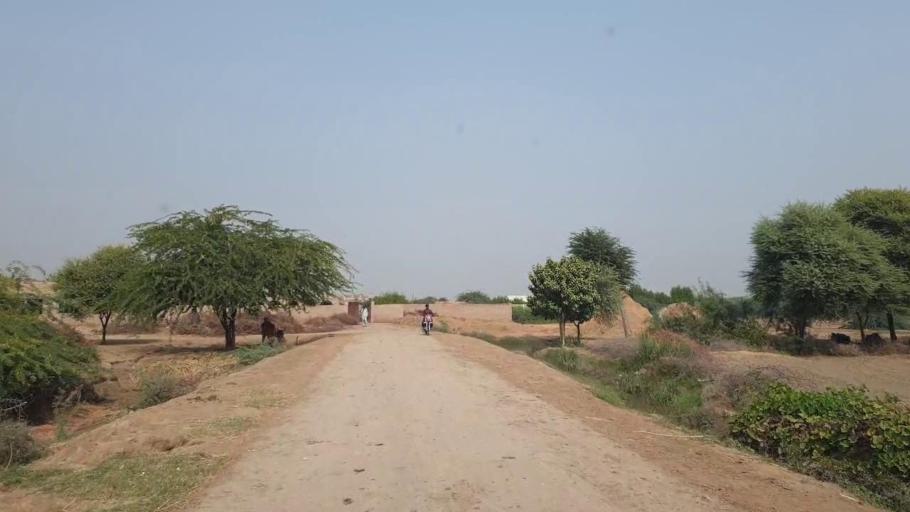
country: PK
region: Sindh
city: Matli
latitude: 25.1516
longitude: 68.7021
